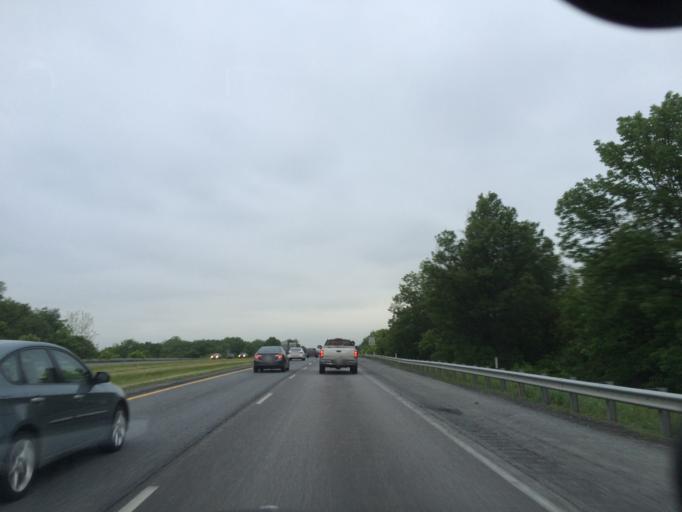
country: US
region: Maryland
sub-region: Washington County
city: Halfway
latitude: 39.6056
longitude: -77.7409
